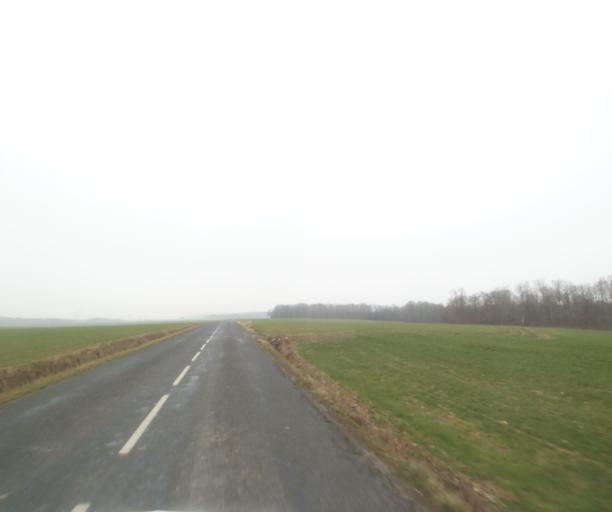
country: FR
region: Champagne-Ardenne
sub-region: Departement de la Haute-Marne
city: Bienville
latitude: 48.5209
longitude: 5.0696
